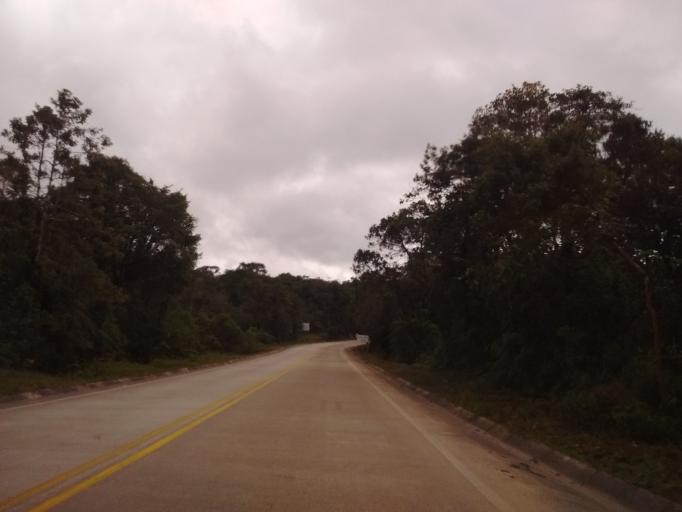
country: CO
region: Huila
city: Isnos
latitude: 2.0436
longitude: -76.2853
